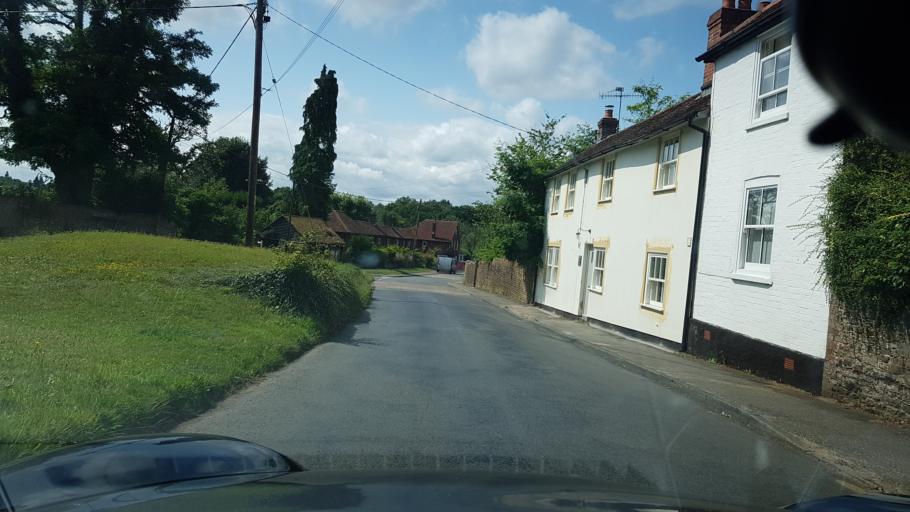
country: GB
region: England
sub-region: Surrey
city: Elstead
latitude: 51.1497
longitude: -0.7119
